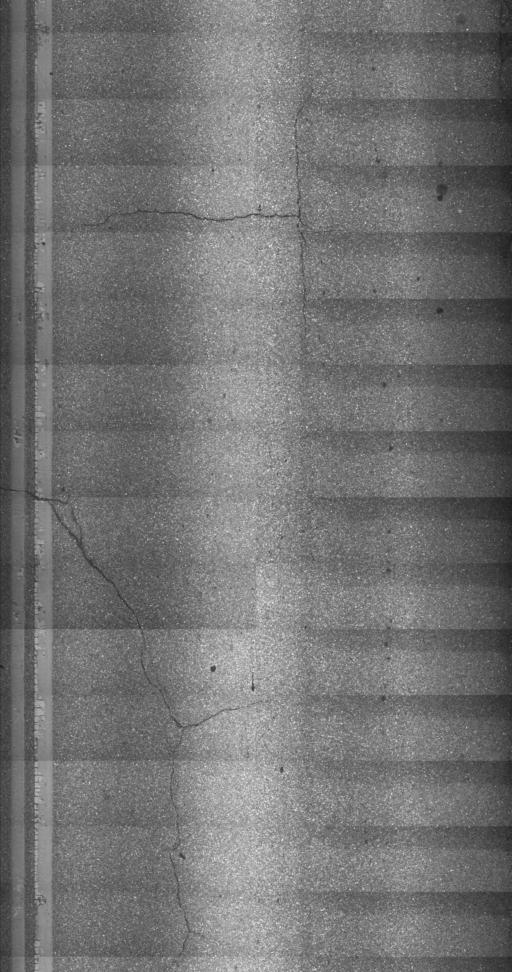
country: US
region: Vermont
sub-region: Bennington County
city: Manchester Center
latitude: 43.1590
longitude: -73.0723
